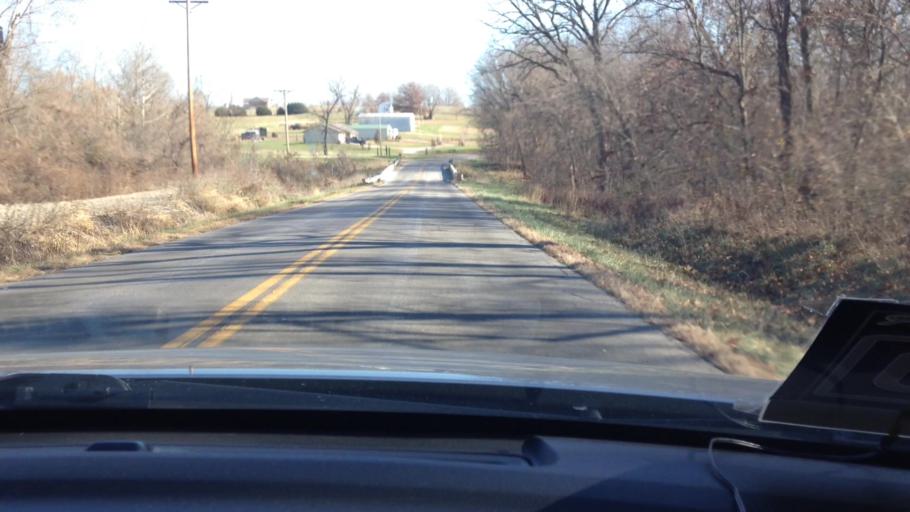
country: US
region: Missouri
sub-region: Platte County
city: Weston
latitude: 39.4981
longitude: -94.8367
